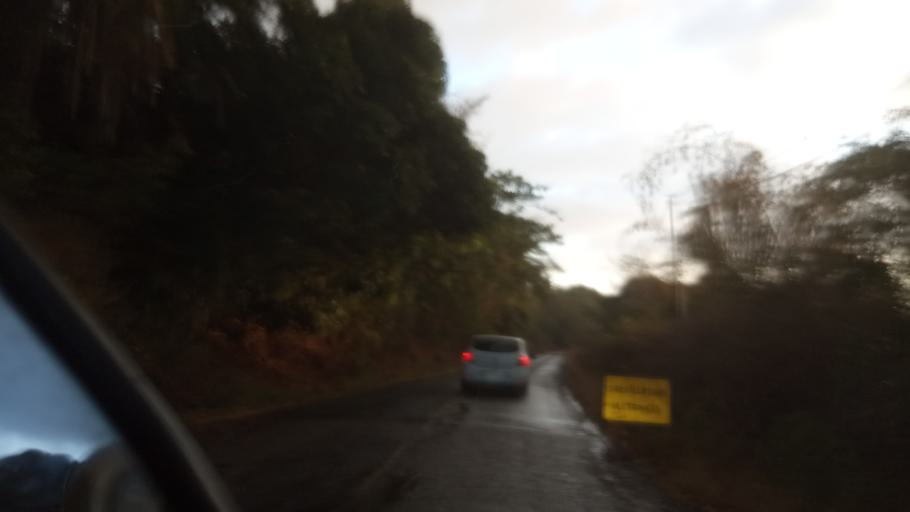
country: YT
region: Kani-Keli
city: Kani Keli
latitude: -12.9354
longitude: 45.1037
